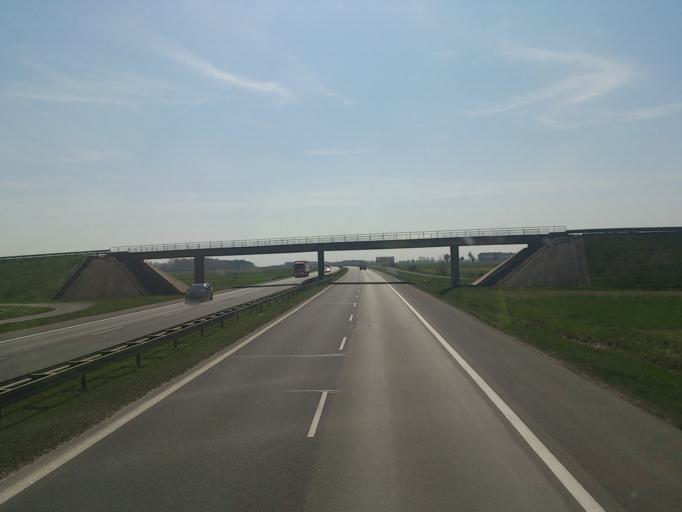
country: PL
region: Lodz Voivodeship
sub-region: Powiat piotrkowski
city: Grabica
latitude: 51.5100
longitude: 19.6022
